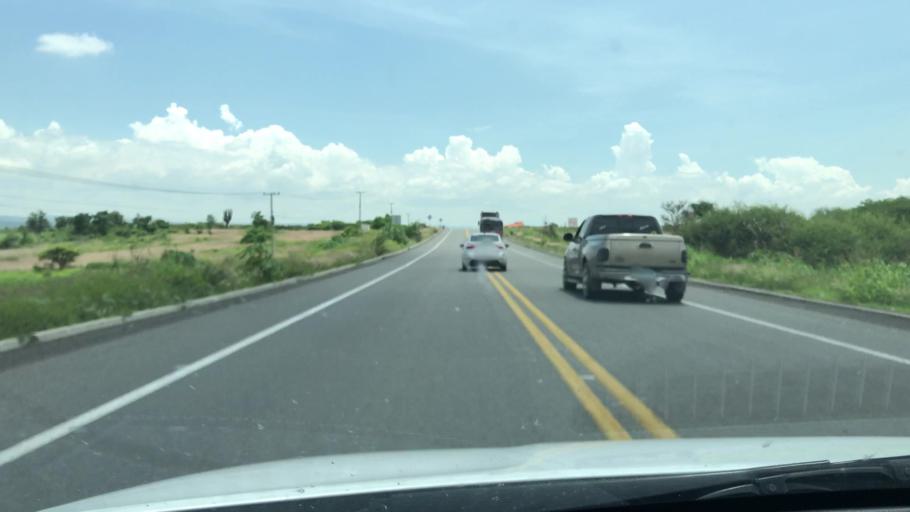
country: MX
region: Jalisco
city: Degollado
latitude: 20.3444
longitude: -102.1605
